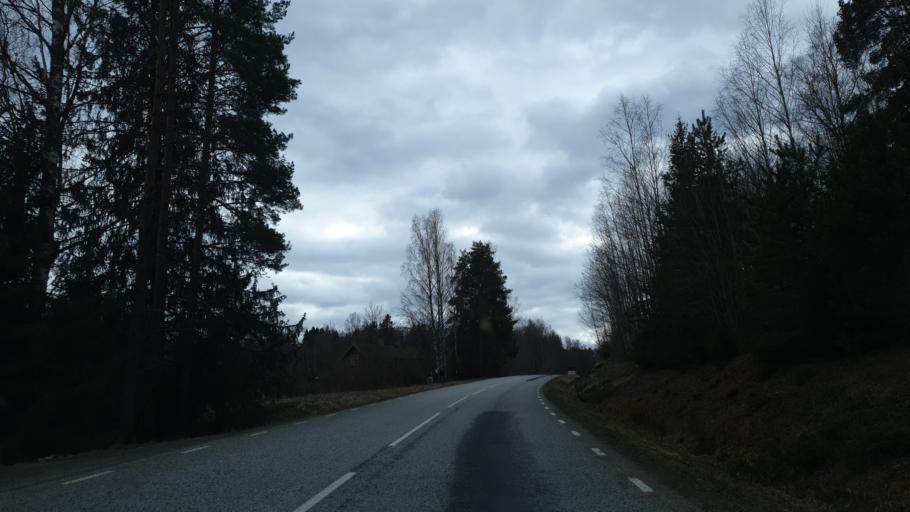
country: SE
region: OErebro
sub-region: Nora Kommun
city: As
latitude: 59.6028
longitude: 14.9252
